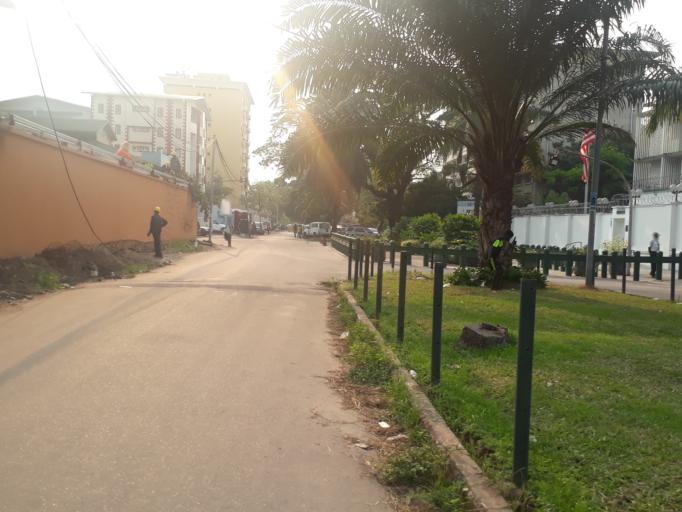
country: CD
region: Kinshasa
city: Kinshasa
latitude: -4.3010
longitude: 15.3140
